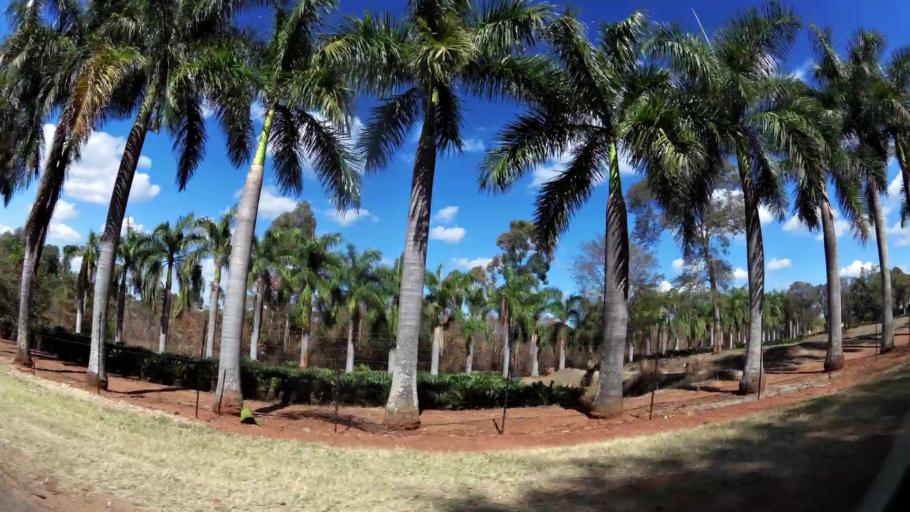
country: ZA
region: Limpopo
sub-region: Mopani District Municipality
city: Tzaneen
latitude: -23.8425
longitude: 30.1475
